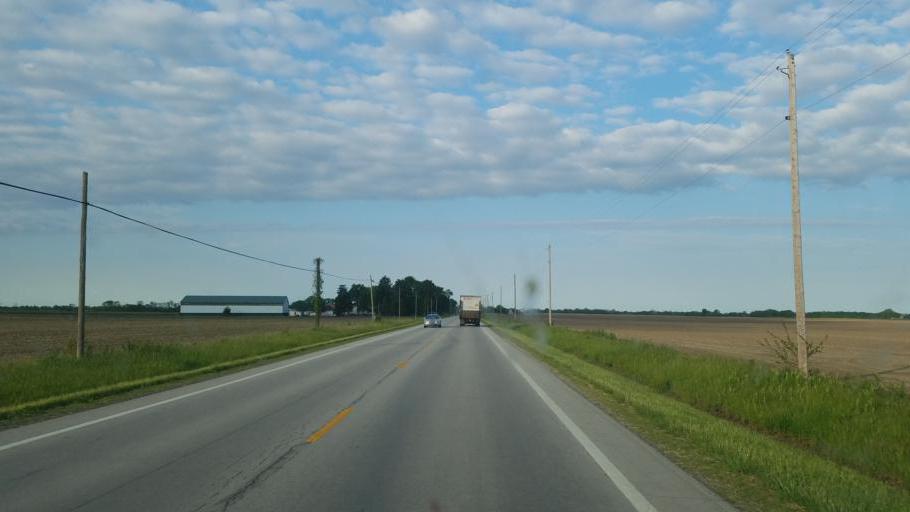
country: US
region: Ohio
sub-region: Madison County
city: Mount Sterling
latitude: 39.6700
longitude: -83.3121
